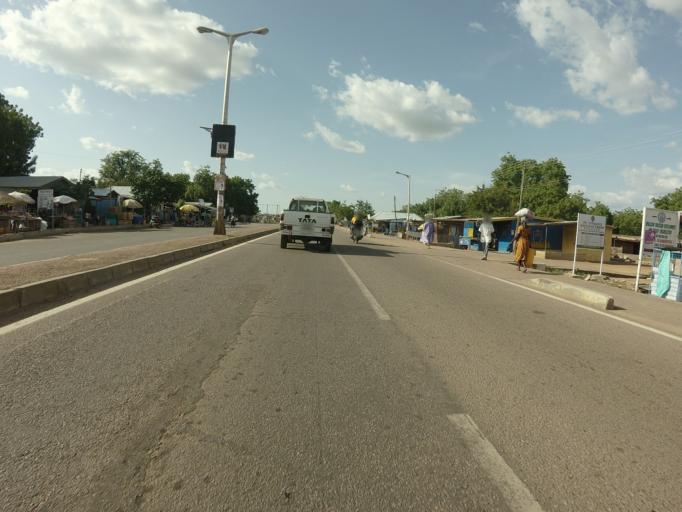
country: GH
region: Upper East
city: Bolgatanga
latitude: 10.7749
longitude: -0.8555
